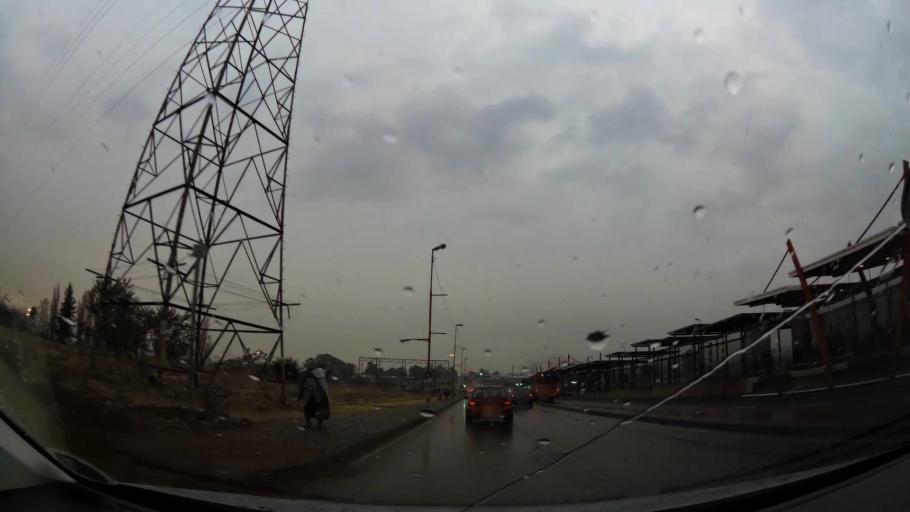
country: ZA
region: Gauteng
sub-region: City of Johannesburg Metropolitan Municipality
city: Soweto
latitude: -26.2629
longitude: 27.8863
